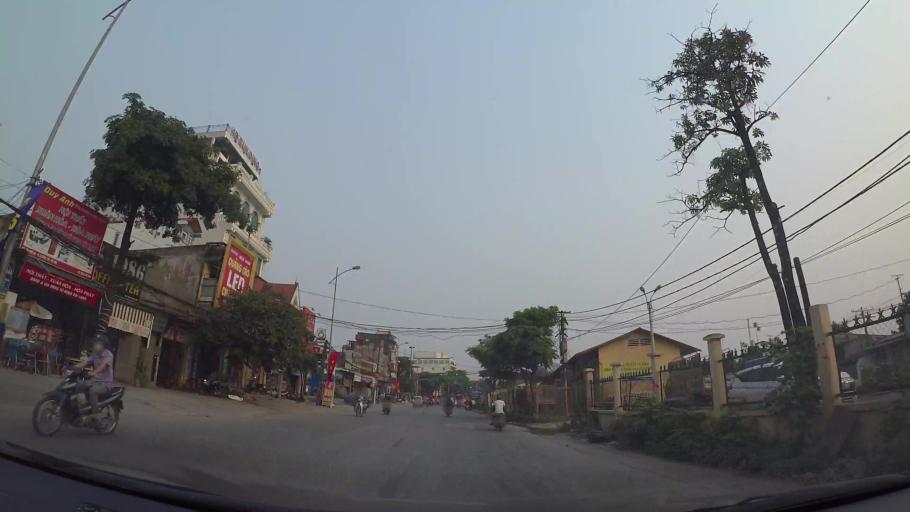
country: VN
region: Ha Noi
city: Thuong Tin
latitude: 20.8724
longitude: 105.8640
